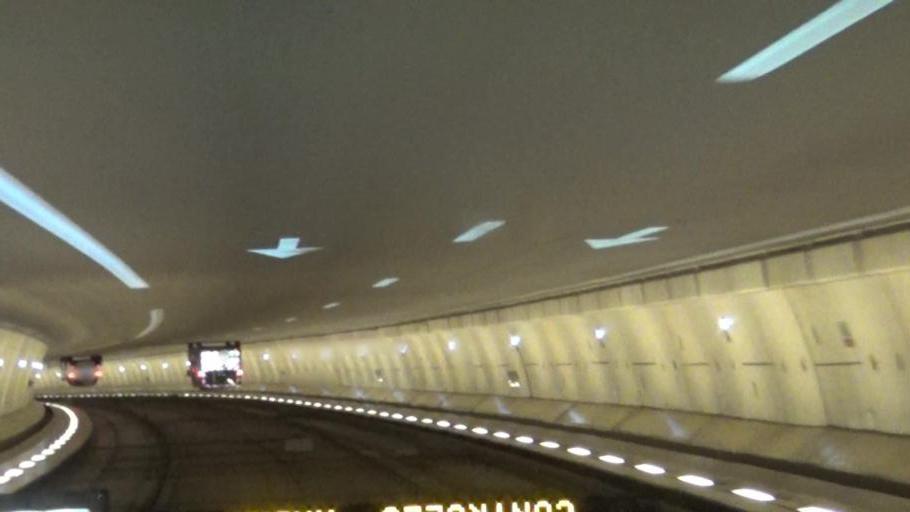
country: FR
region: Ile-de-France
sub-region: Departement des Yvelines
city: Bougival
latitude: 48.8635
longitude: 2.1597
